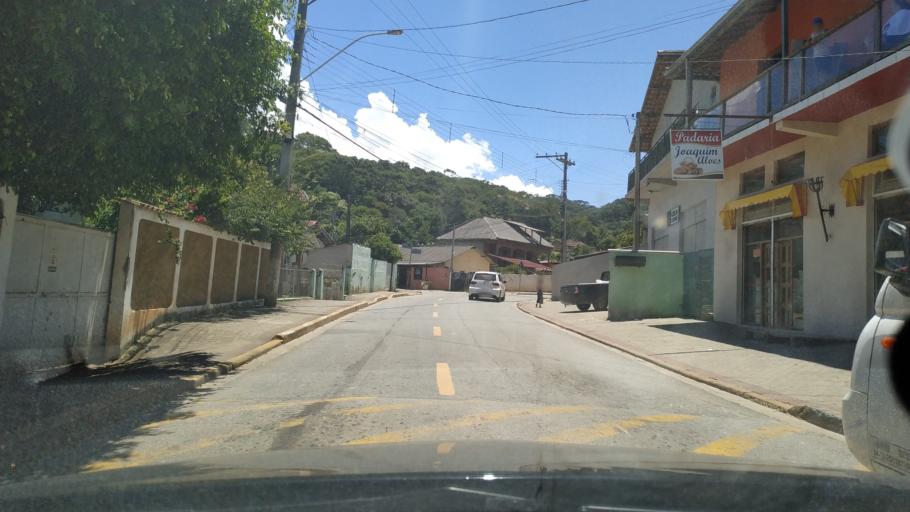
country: BR
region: Sao Paulo
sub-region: Campos Do Jordao
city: Campos do Jordao
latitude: -22.8224
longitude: -45.6761
